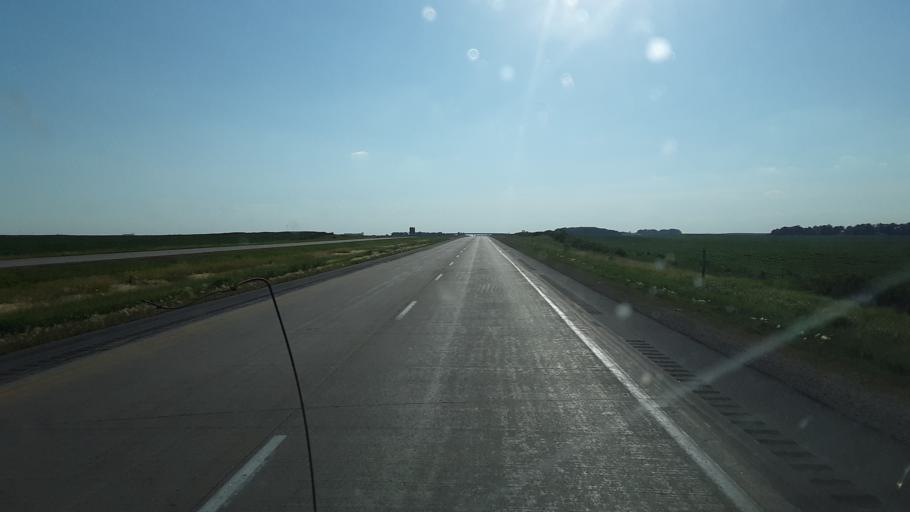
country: US
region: Iowa
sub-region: Hardin County
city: Iowa Falls
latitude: 42.4482
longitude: -93.2824
